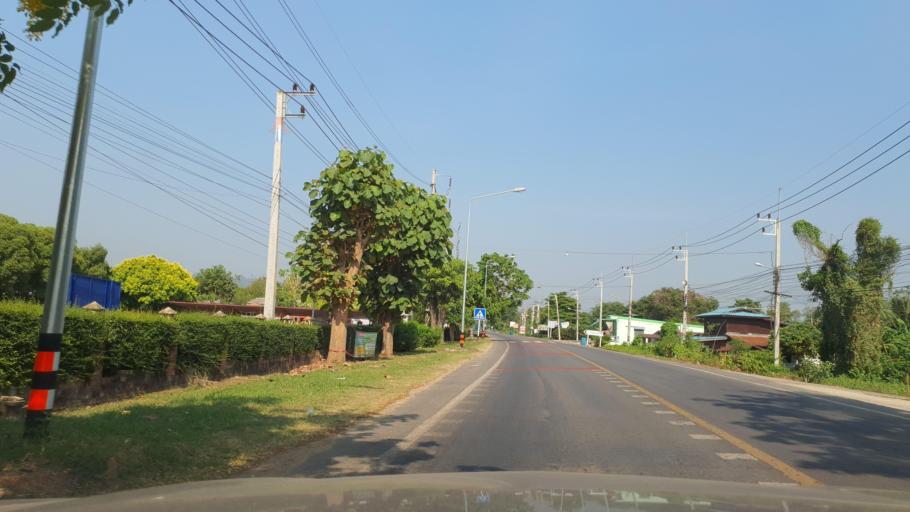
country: TH
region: Kanchanaburi
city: Kanchanaburi
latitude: 14.0357
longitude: 99.4936
